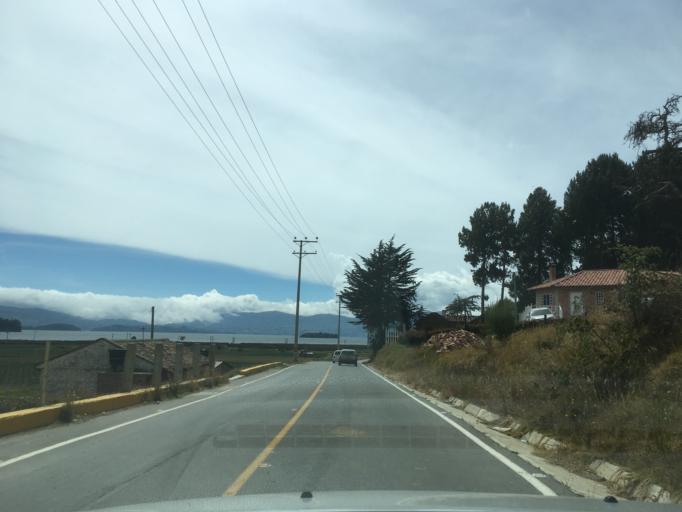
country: CO
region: Boyaca
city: Aquitania
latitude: 5.5994
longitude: -72.9135
